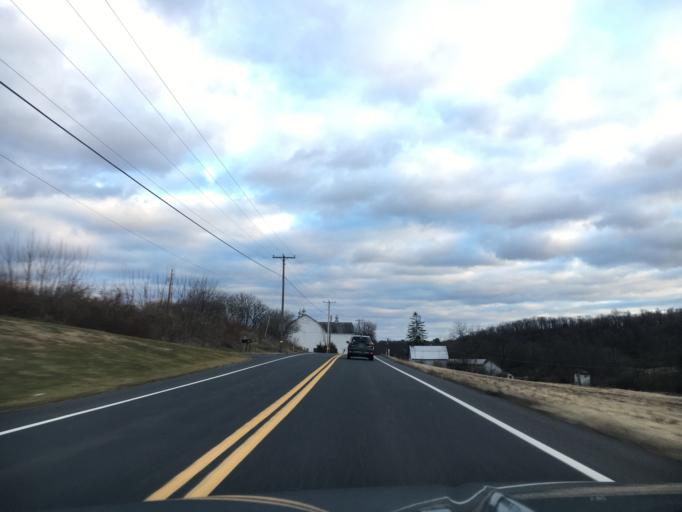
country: US
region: Pennsylvania
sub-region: Lehigh County
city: Schnecksville
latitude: 40.6810
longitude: -75.6540
